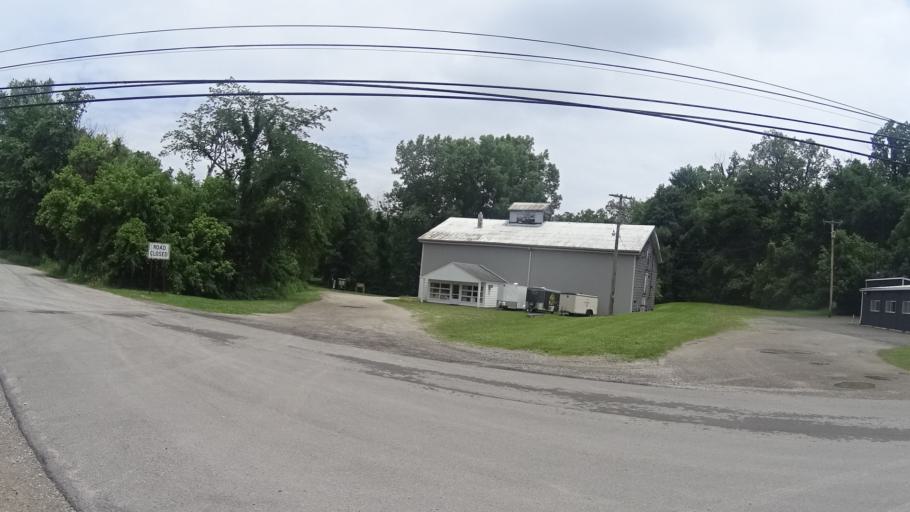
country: US
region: Ohio
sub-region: Erie County
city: Milan
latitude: 41.2997
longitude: -82.6084
